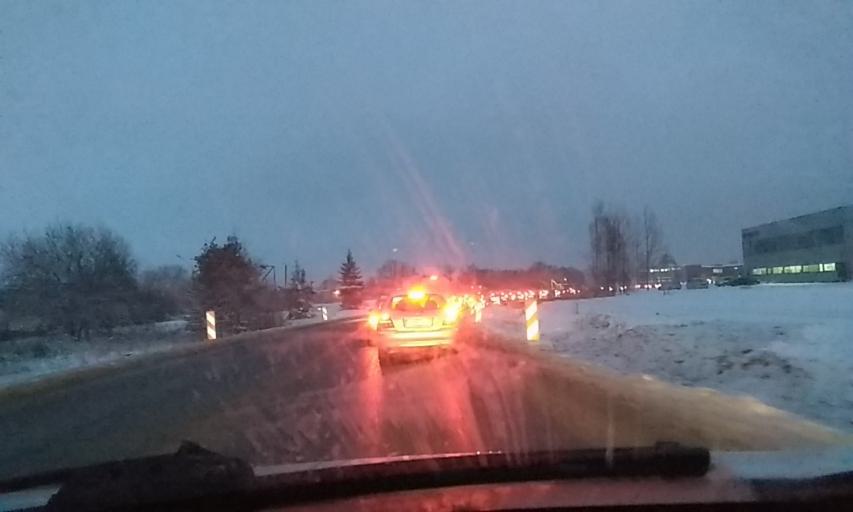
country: LT
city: Ramuciai
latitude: 54.9045
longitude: 24.0285
